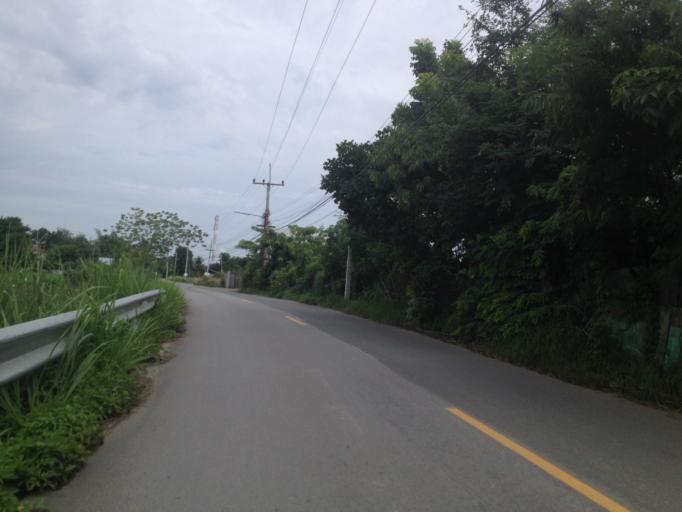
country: TH
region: Chiang Mai
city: Hang Dong
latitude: 18.7074
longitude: 98.9569
